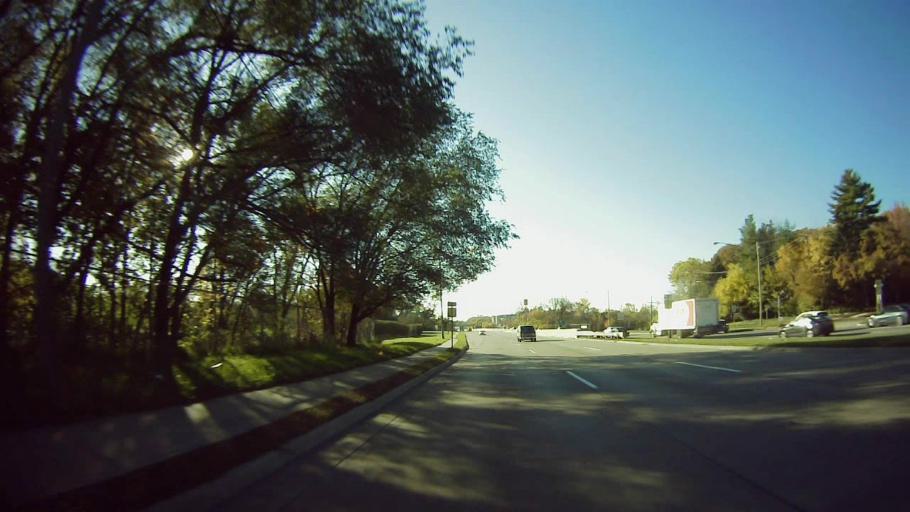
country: US
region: Michigan
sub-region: Wayne County
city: Dearborn Heights
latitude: 42.3034
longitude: -83.2719
